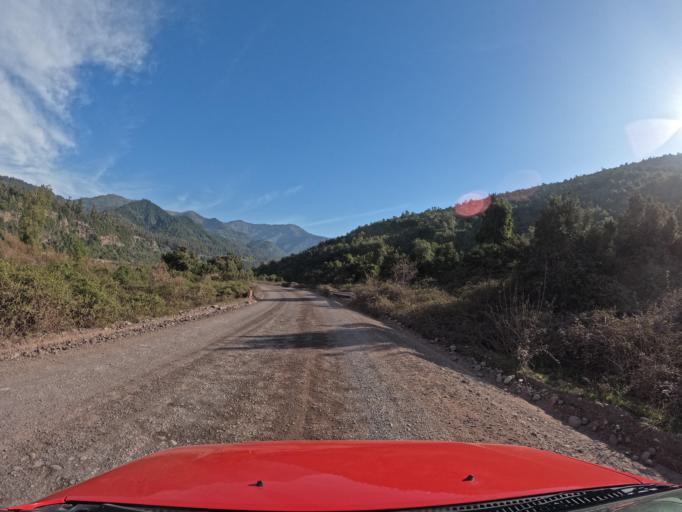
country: CL
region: O'Higgins
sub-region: Provincia de Colchagua
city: Chimbarongo
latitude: -34.9982
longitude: -70.8254
